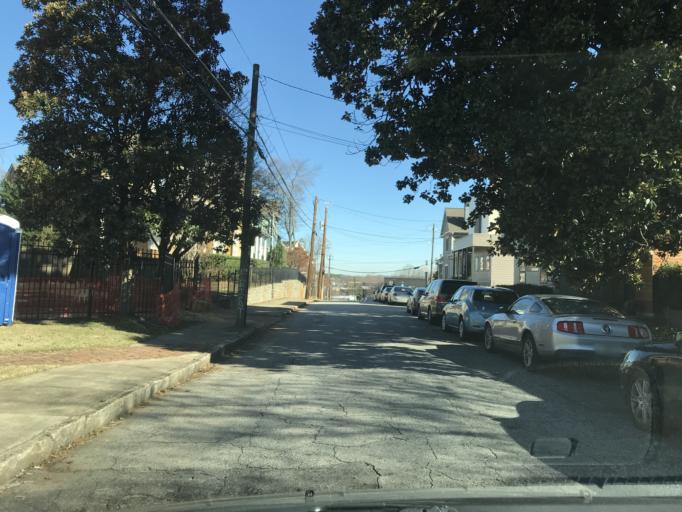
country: US
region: Georgia
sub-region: Fulton County
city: Atlanta
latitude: 33.7559
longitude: -84.3678
